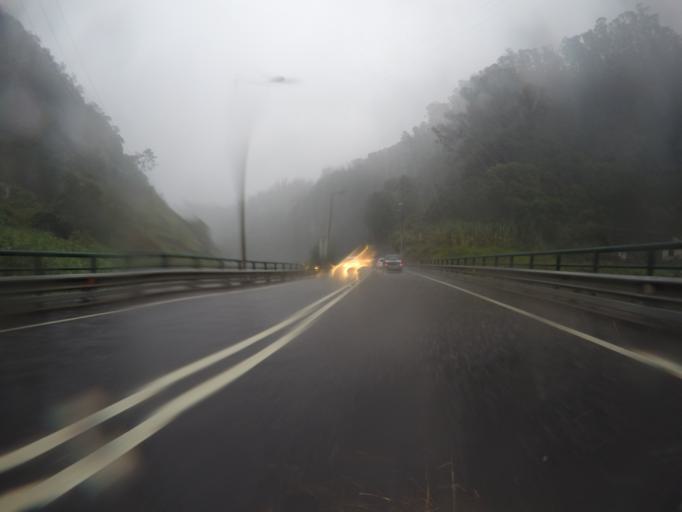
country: PT
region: Madeira
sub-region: Santa Cruz
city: Santa Cruz
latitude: 32.7357
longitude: -16.8080
